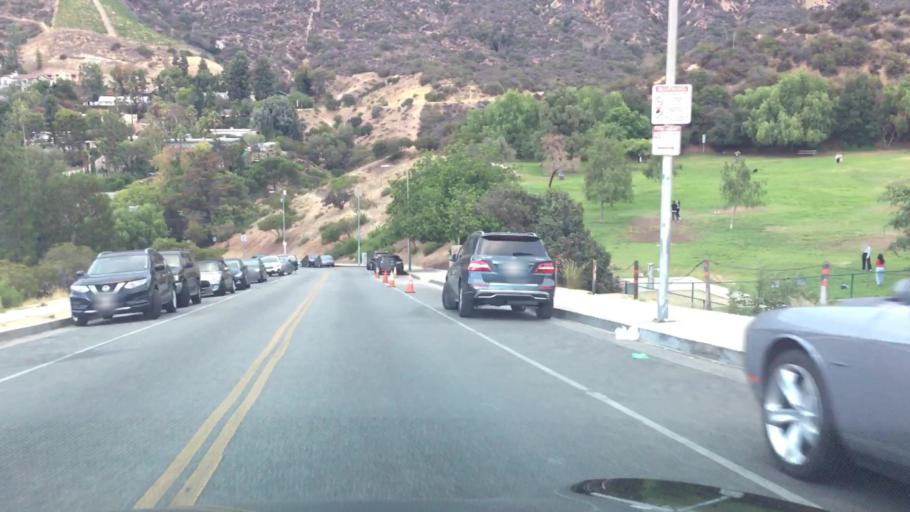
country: US
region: California
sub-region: Los Angeles County
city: Hollywood
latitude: 34.1263
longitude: -118.3265
